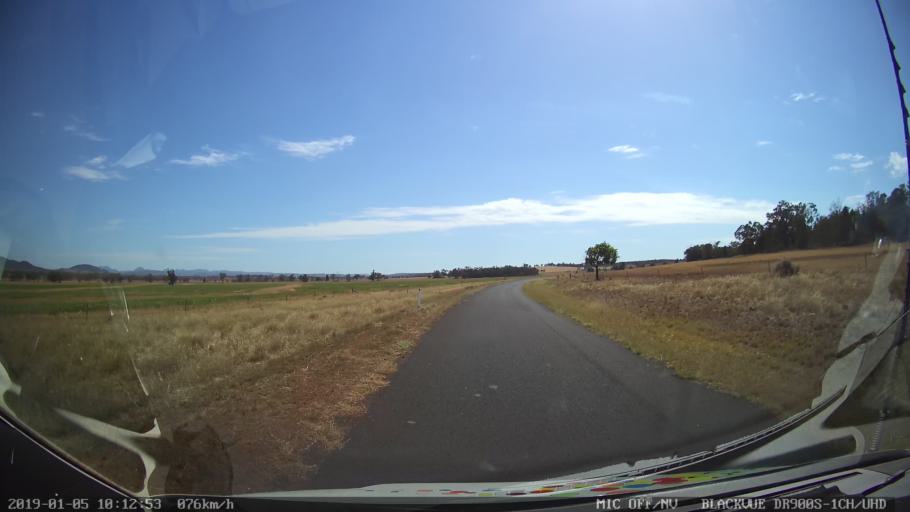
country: AU
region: New South Wales
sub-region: Gilgandra
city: Gilgandra
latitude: -31.6047
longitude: 148.9180
